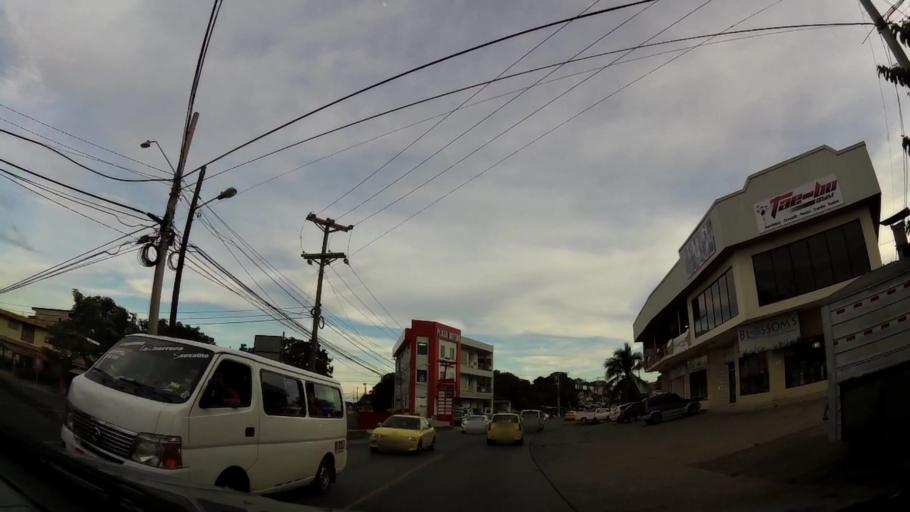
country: PA
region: Panama
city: La Chorrera
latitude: 8.8776
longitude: -79.7801
